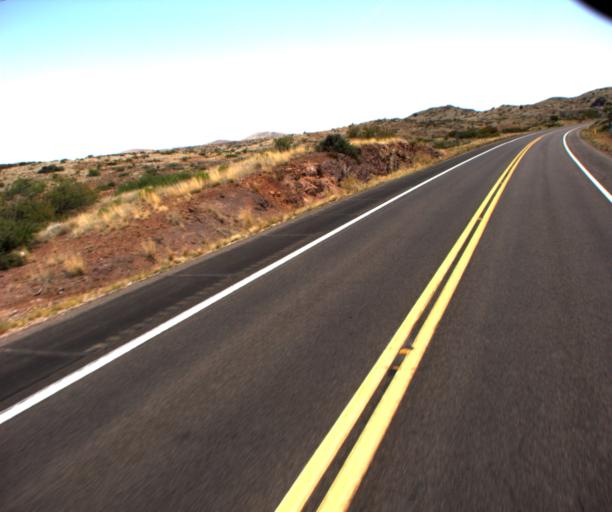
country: US
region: Arizona
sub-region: Greenlee County
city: Clifton
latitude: 32.7602
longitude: -109.2455
